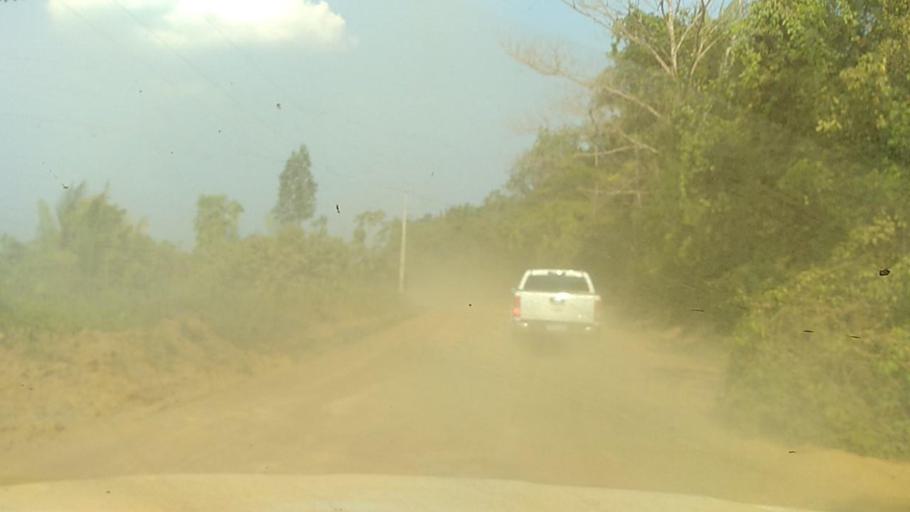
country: BR
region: Rondonia
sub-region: Porto Velho
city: Porto Velho
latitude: -8.6706
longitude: -63.9987
